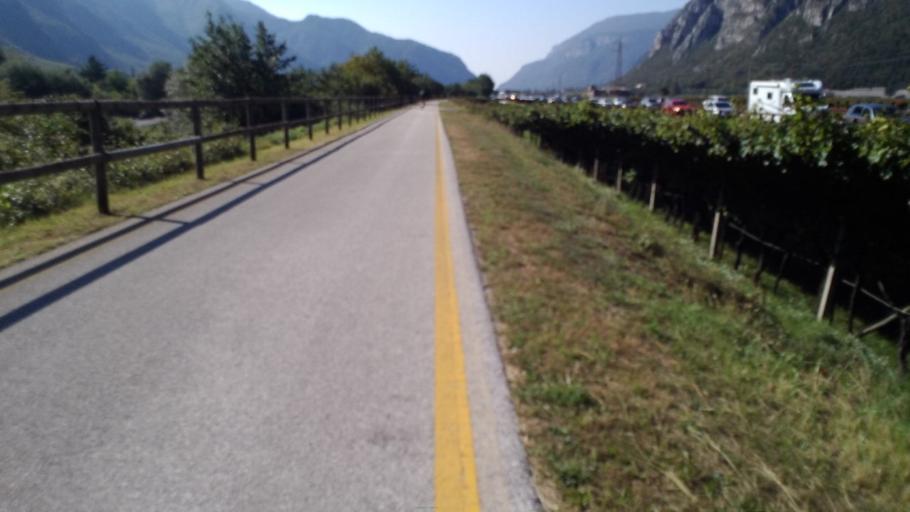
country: IT
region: Trentino-Alto Adige
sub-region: Provincia di Trento
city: Avio
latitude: 45.7245
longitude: 10.9387
